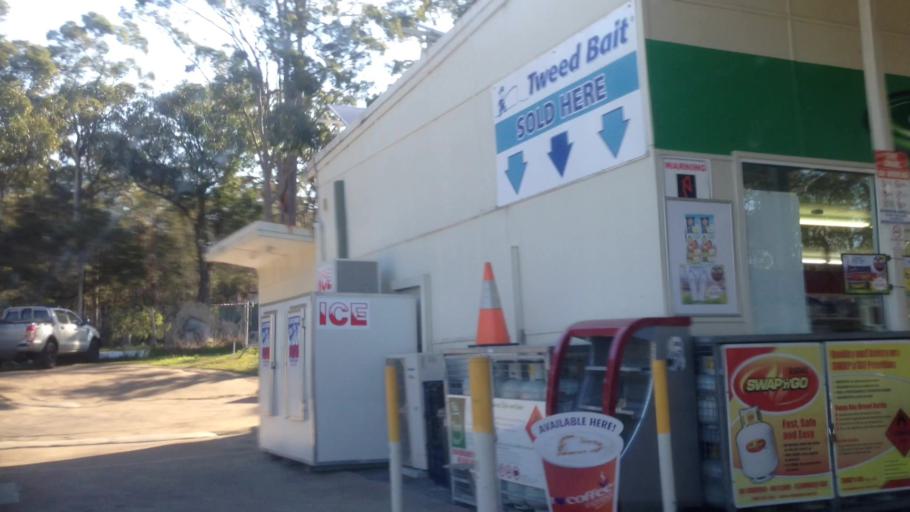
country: AU
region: New South Wales
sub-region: Lake Macquarie Shire
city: Dora Creek
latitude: -33.1081
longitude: 151.4982
